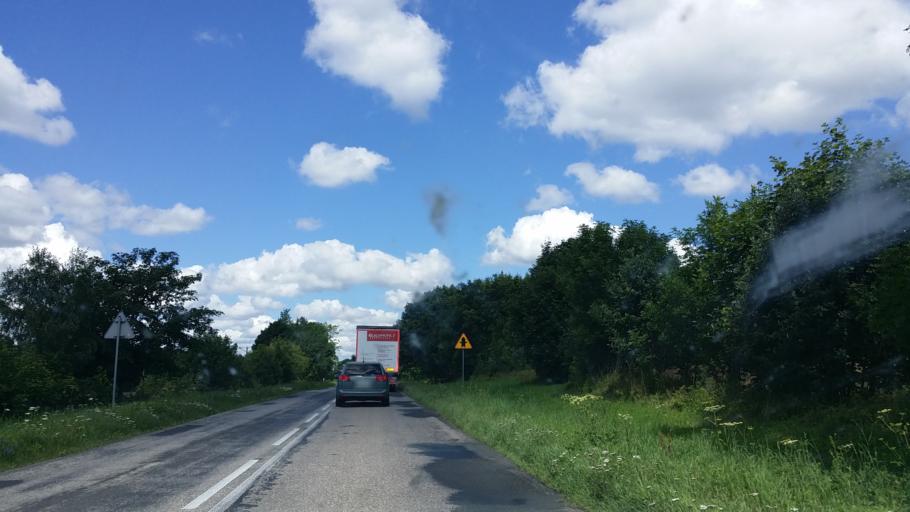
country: PL
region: West Pomeranian Voivodeship
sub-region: Powiat swidwinski
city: Swidwin
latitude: 53.8335
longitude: 15.7480
